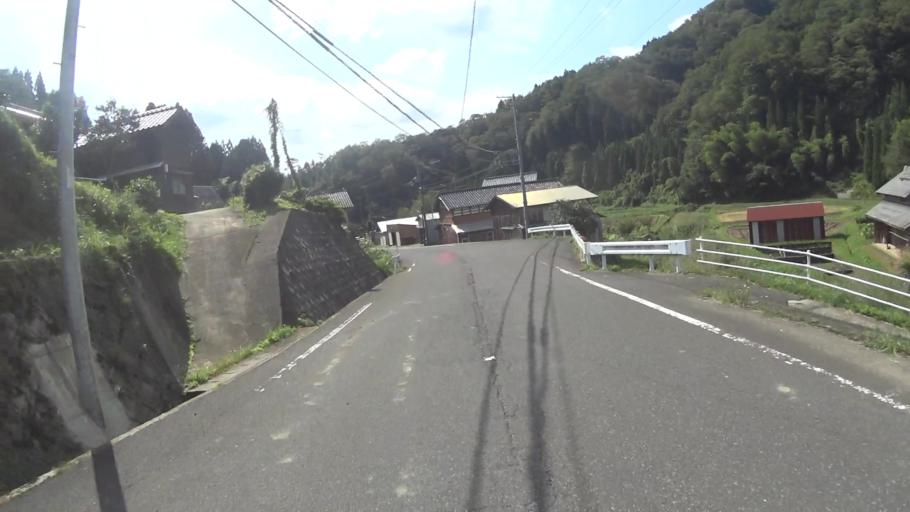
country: JP
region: Kyoto
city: Miyazu
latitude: 35.6959
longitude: 135.1721
